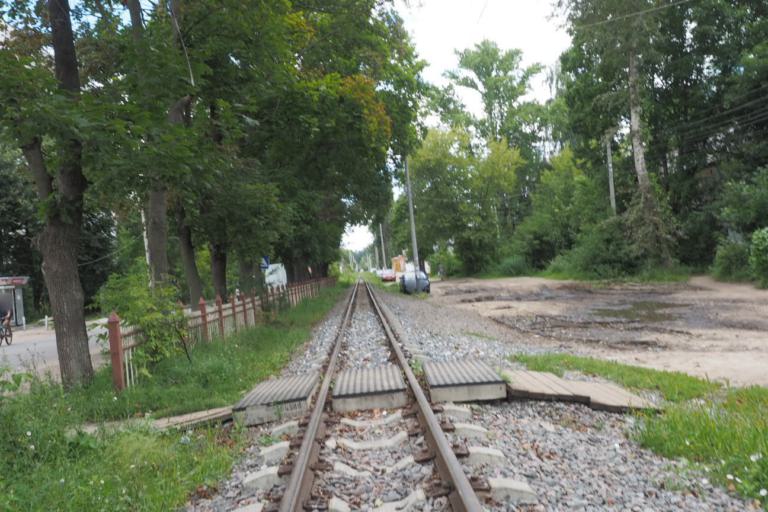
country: RU
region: Moskovskaya
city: Zhukovskiy
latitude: 55.5882
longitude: 38.1422
